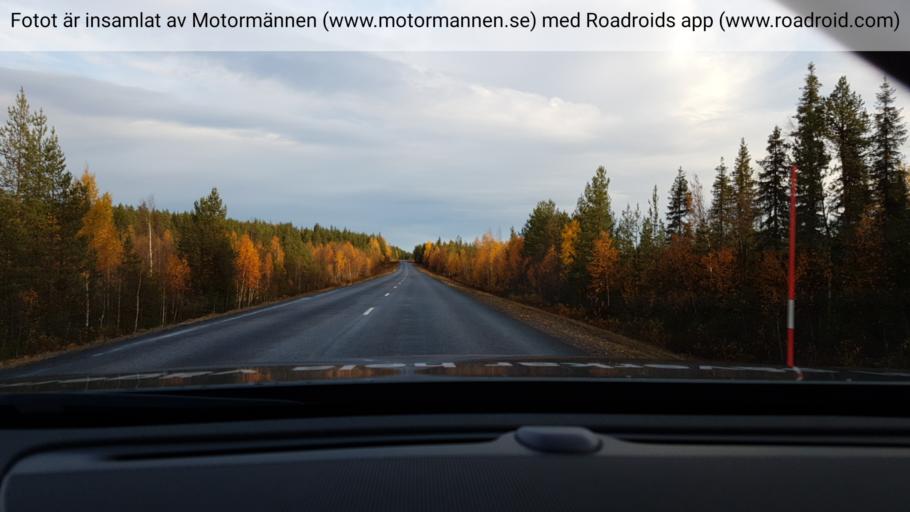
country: SE
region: Norrbotten
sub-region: Overkalix Kommun
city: OEverkalix
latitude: 66.9911
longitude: 22.5870
